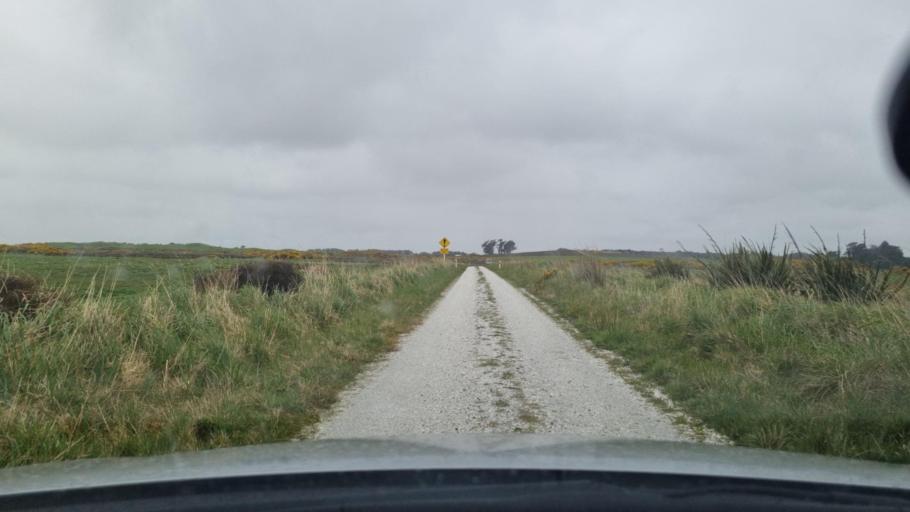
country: NZ
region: Southland
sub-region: Invercargill City
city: Bluff
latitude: -46.5202
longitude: 168.2797
